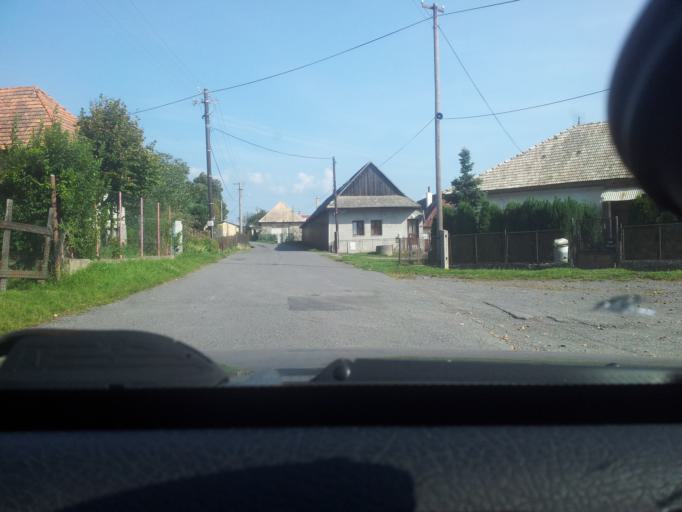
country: SK
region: Banskobystricky
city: Zarnovica
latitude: 48.4119
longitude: 18.7921
